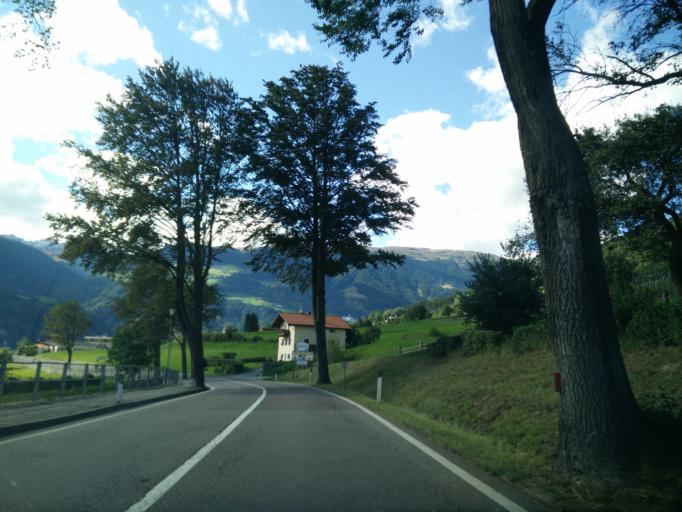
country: IT
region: Trentino-Alto Adige
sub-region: Bolzano
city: Malles Venosta
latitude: 46.6841
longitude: 10.5581
